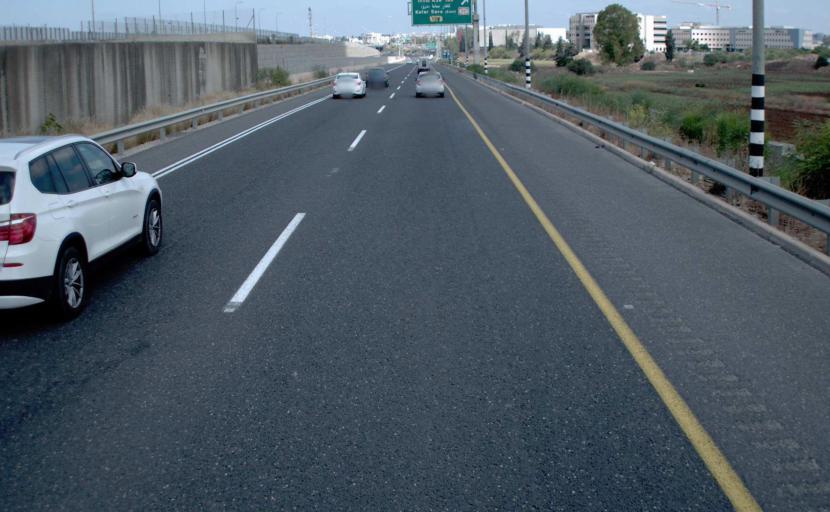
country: IL
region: Central District
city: Jaljulya
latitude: 32.1583
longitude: 34.9341
